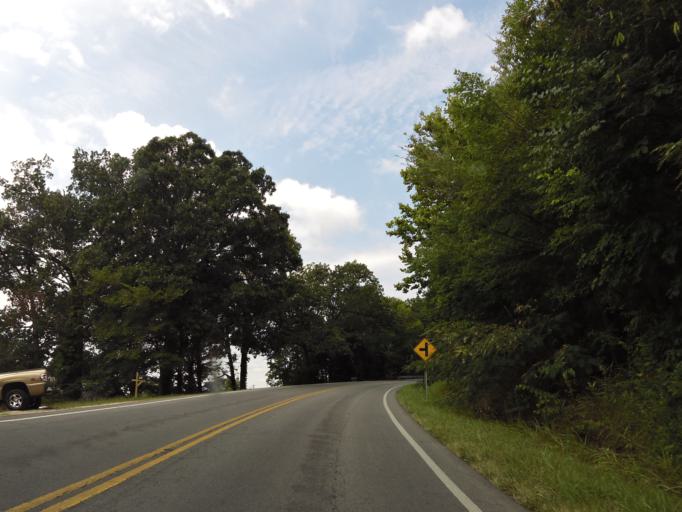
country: US
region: Tennessee
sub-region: Decatur County
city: Decaturville
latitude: 35.6165
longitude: -88.0163
